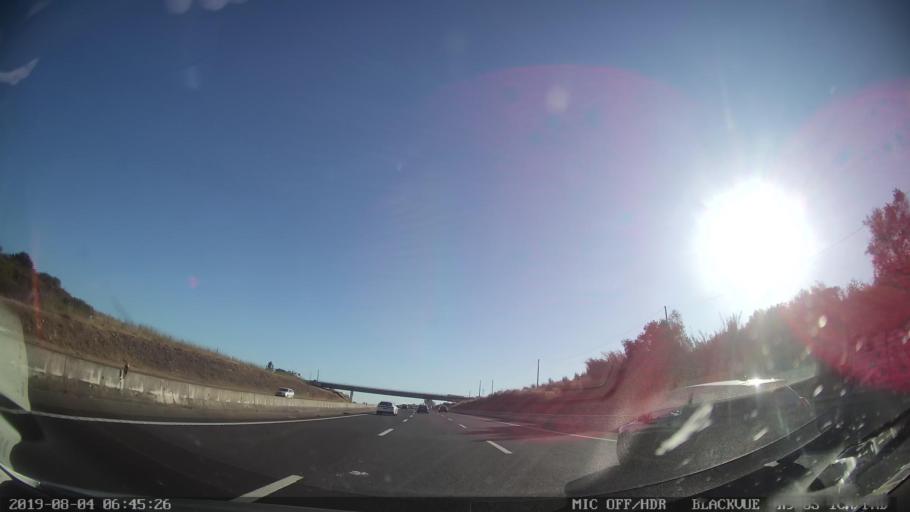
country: PT
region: Santarem
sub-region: Santarem
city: Santarem
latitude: 39.2361
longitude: -8.7602
